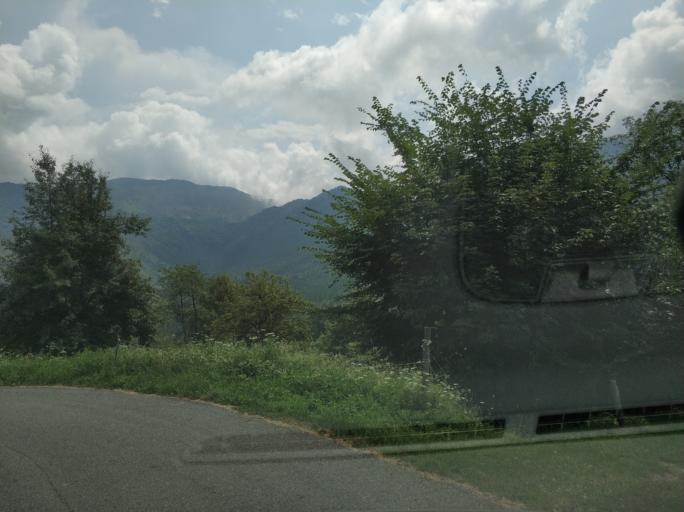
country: IT
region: Piedmont
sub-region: Provincia di Torino
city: Viu
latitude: 45.1989
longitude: 7.3816
